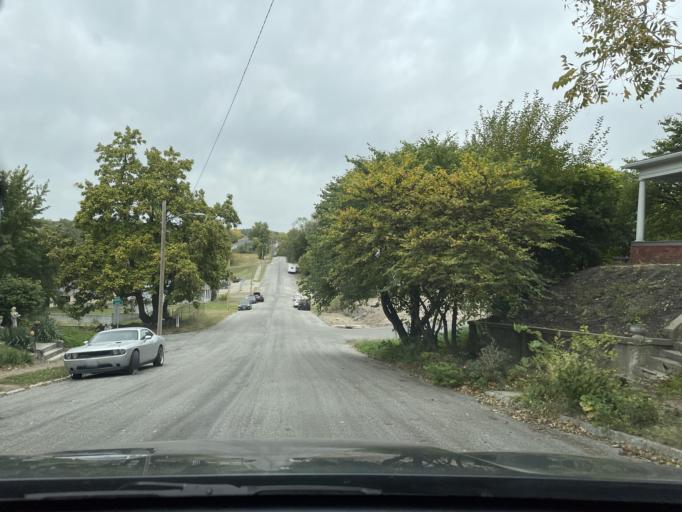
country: US
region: Missouri
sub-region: Buchanan County
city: Saint Joseph
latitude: 39.7719
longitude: -94.8542
